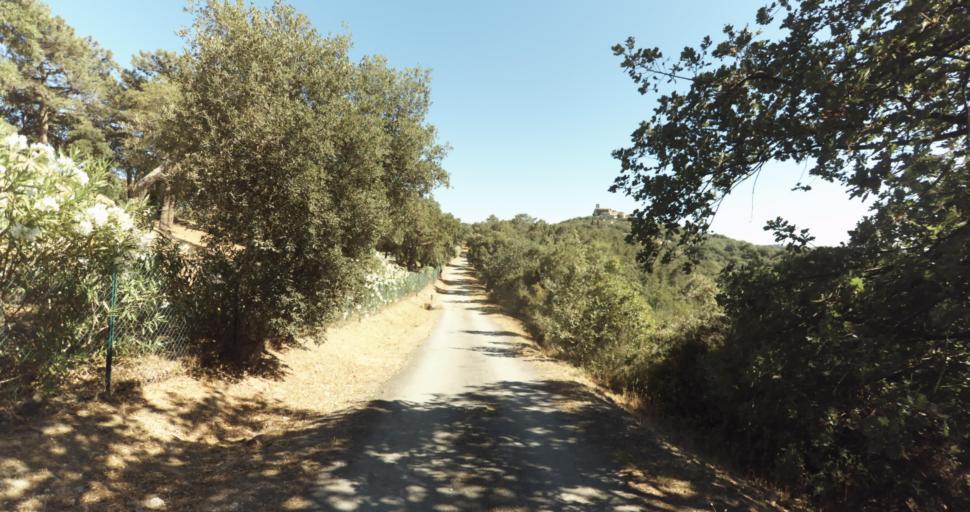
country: FR
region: Provence-Alpes-Cote d'Azur
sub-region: Departement du Var
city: Gassin
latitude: 43.2360
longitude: 6.5846
